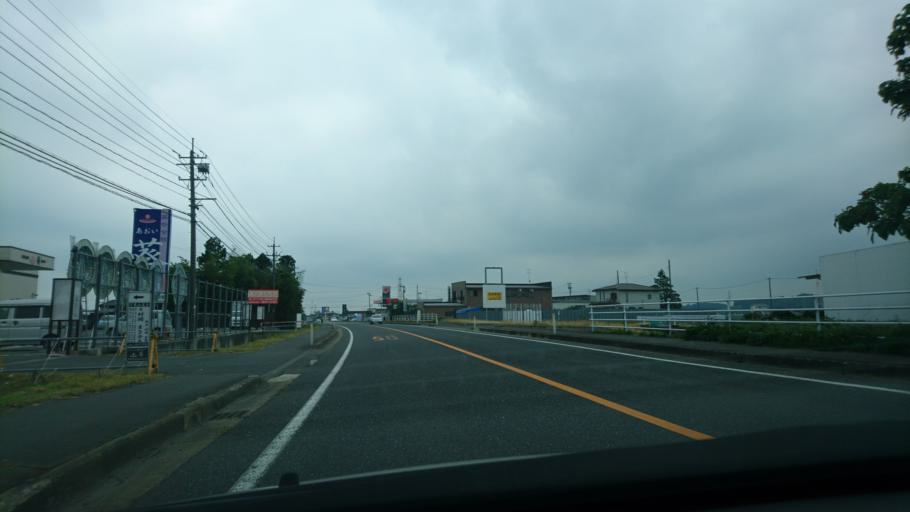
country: JP
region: Miyagi
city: Furukawa
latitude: 38.6441
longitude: 140.8790
